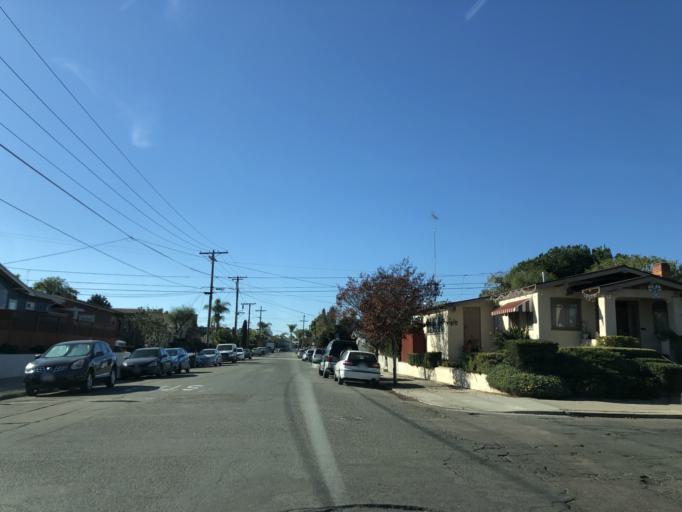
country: US
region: California
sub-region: San Diego County
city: San Diego
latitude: 32.7421
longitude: -117.1271
